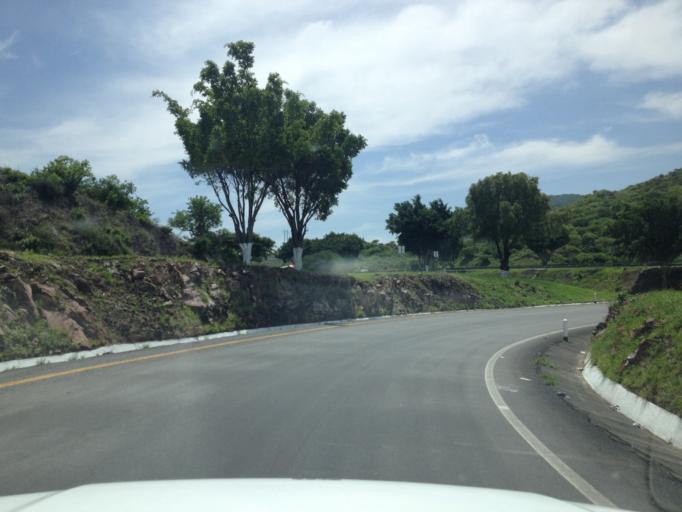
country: MX
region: Michoacan
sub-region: Cuitzeo
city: San Juan Benito Juarez (San Juan Tararameo)
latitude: 19.8991
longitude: -101.1462
